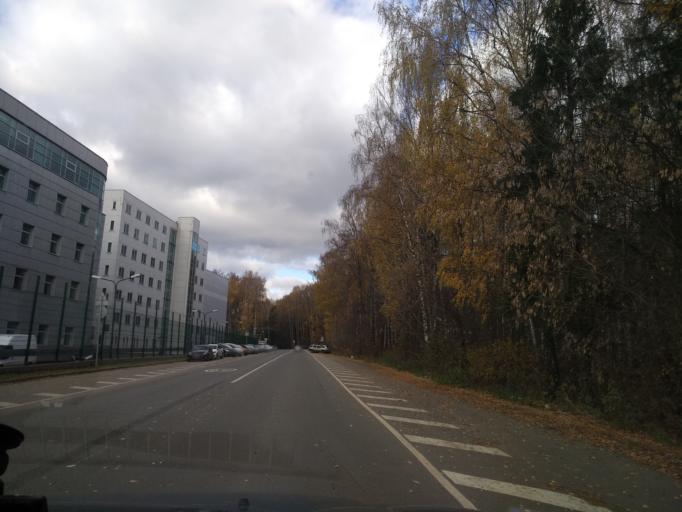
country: RU
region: Moscow
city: Bibirevo
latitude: 55.9059
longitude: 37.6123
